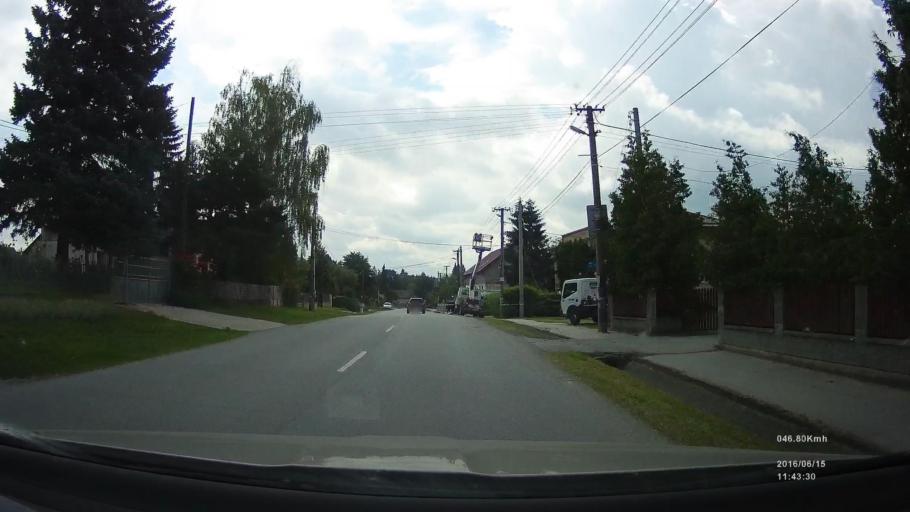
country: SK
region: Kosicky
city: Kosice
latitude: 48.7514
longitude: 21.3440
